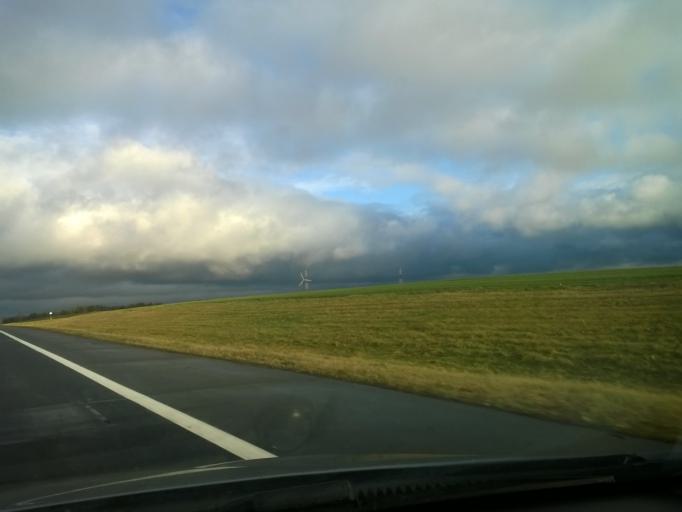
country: BY
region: Minsk
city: Snow
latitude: 53.2590
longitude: 26.2519
